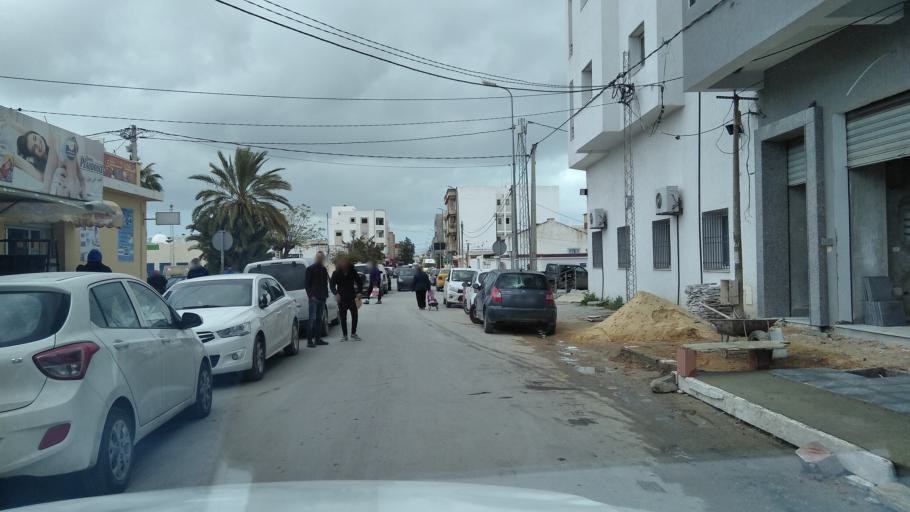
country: TN
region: Bin 'Arus
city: Ben Arous
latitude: 36.7561
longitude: 10.2218
